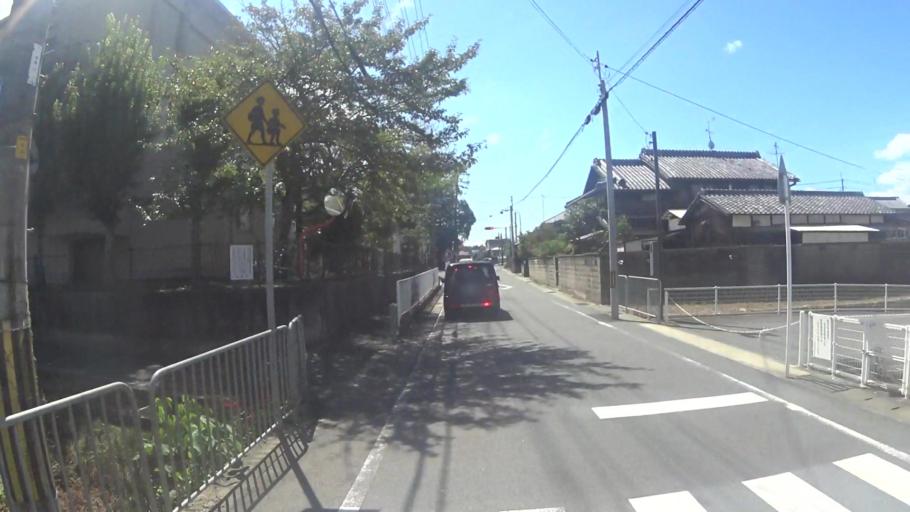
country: JP
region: Kyoto
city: Tanabe
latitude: 34.8303
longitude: 135.8031
